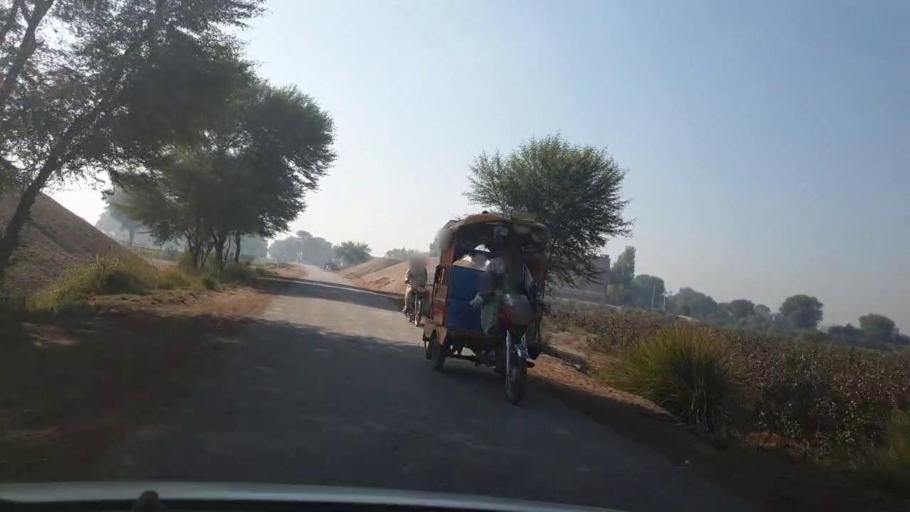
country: PK
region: Sindh
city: Dadu
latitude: 26.6513
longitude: 67.8222
